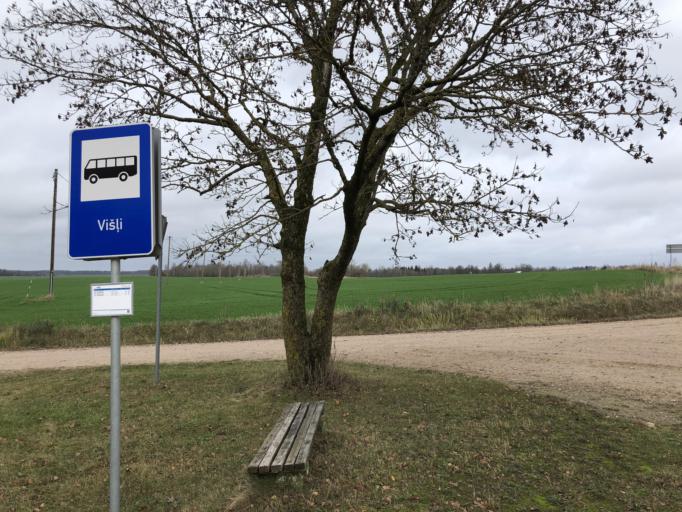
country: LV
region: Talsu Rajons
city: Sabile
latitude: 57.0080
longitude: 22.4882
